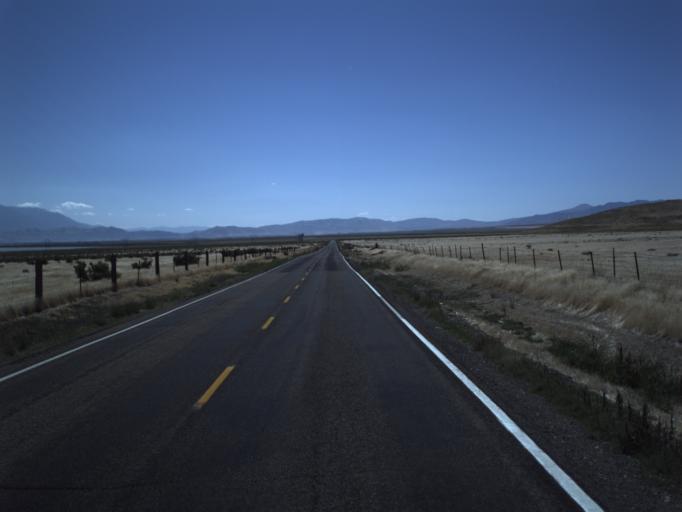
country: US
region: Utah
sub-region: Utah County
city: Eagle Mountain
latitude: 40.1559
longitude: -111.9496
